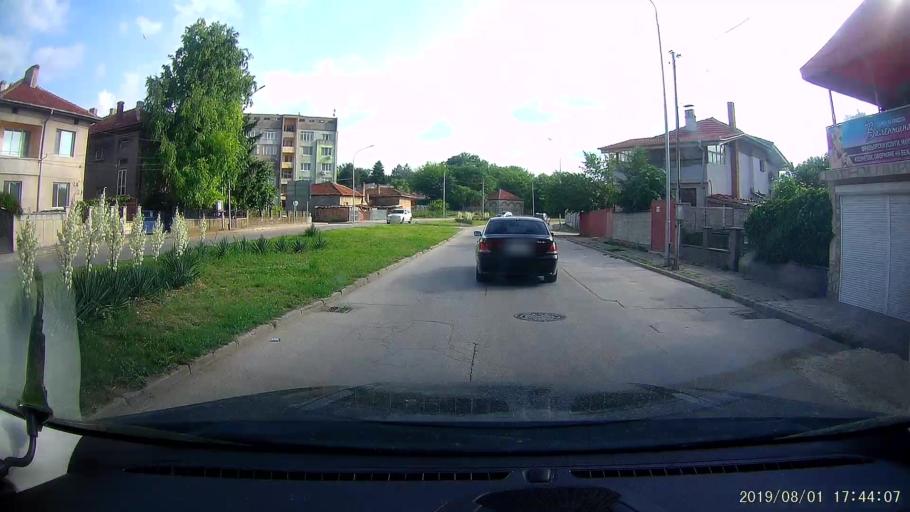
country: BG
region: Silistra
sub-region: Obshtina Silistra
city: Silistra
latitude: 44.1110
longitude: 27.2714
